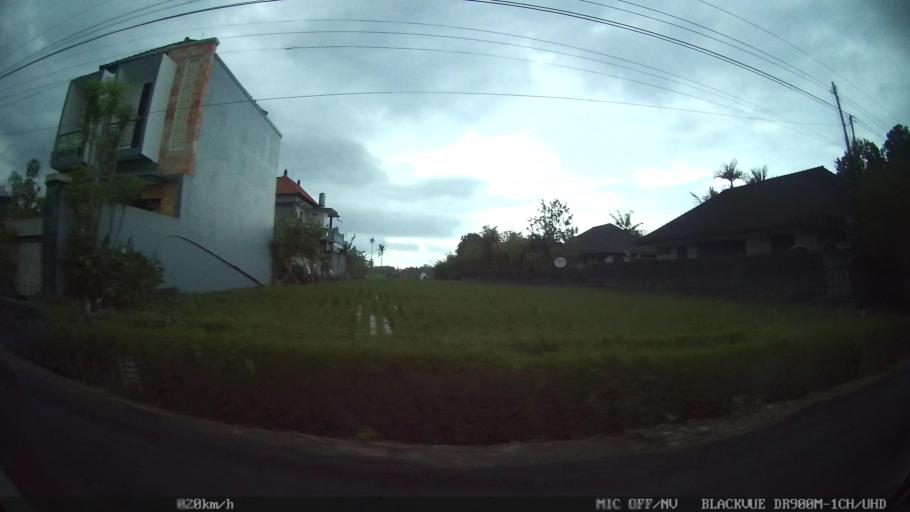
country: ID
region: Bali
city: Banjar Pasekan
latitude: -8.6171
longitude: 115.2980
